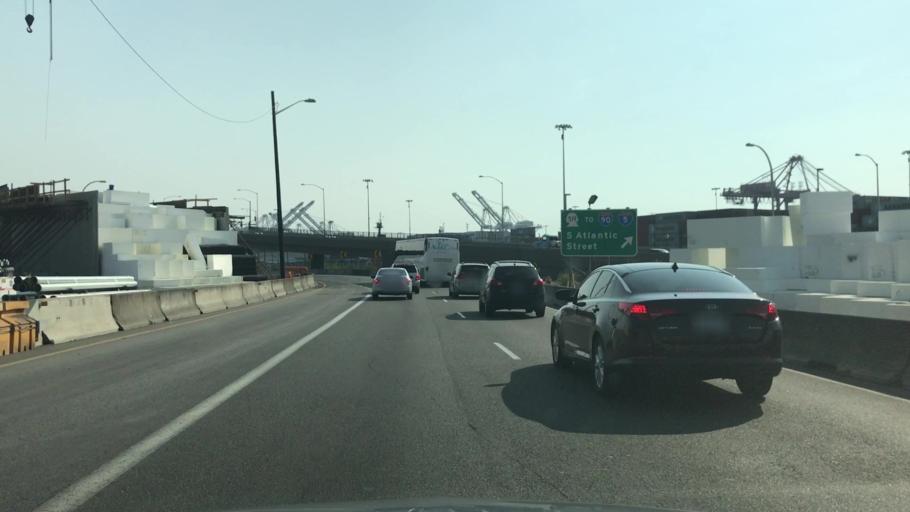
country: US
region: Washington
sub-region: King County
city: Seattle
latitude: 47.5948
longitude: -122.3354
